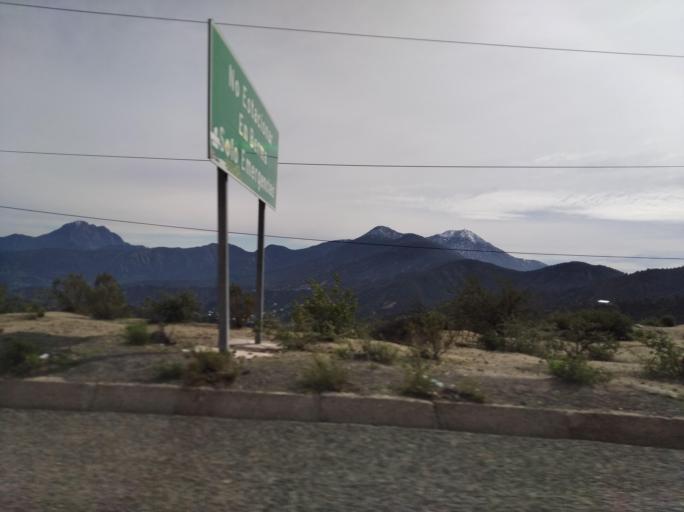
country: CL
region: Valparaiso
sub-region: Provincia de San Felipe
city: Llaillay
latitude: -33.0651
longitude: -71.0152
